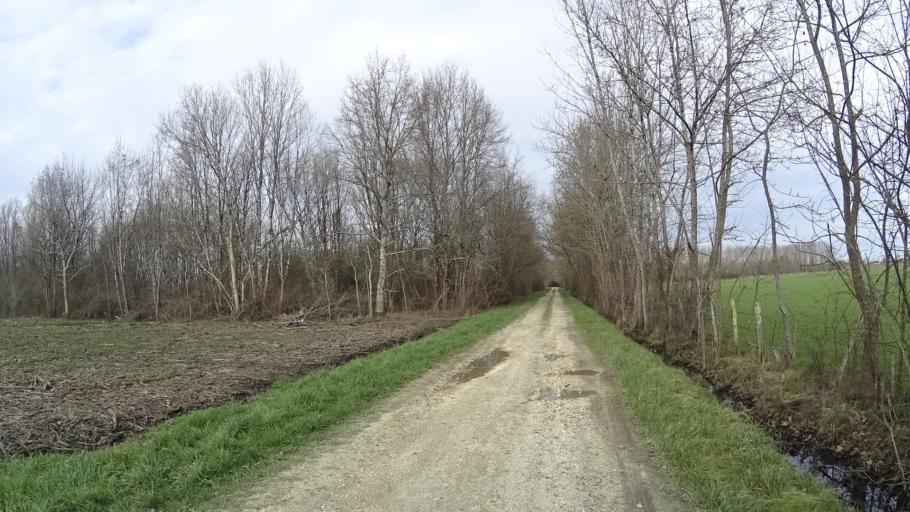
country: FR
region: Aquitaine
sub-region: Departement de la Dordogne
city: Saint-Aulaye
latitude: 45.2116
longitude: 0.1384
